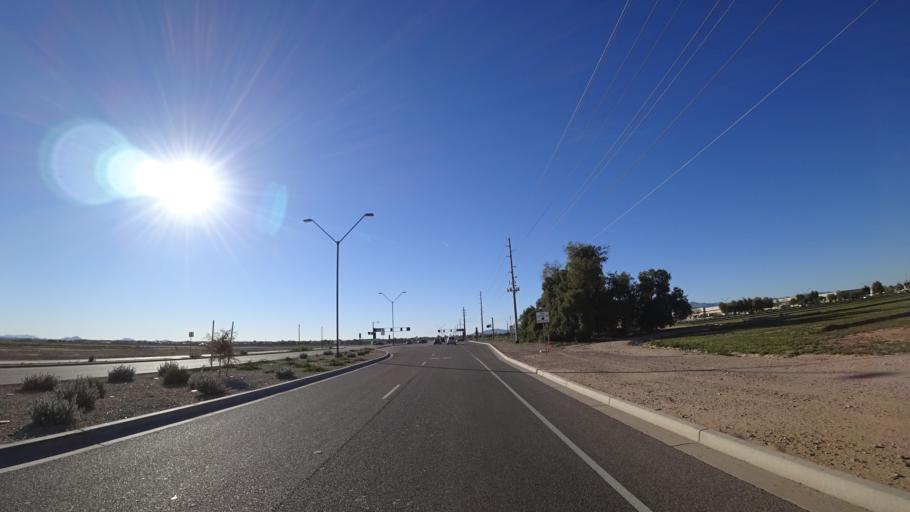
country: US
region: Arizona
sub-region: Maricopa County
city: Goodyear
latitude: 33.4500
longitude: -112.3734
